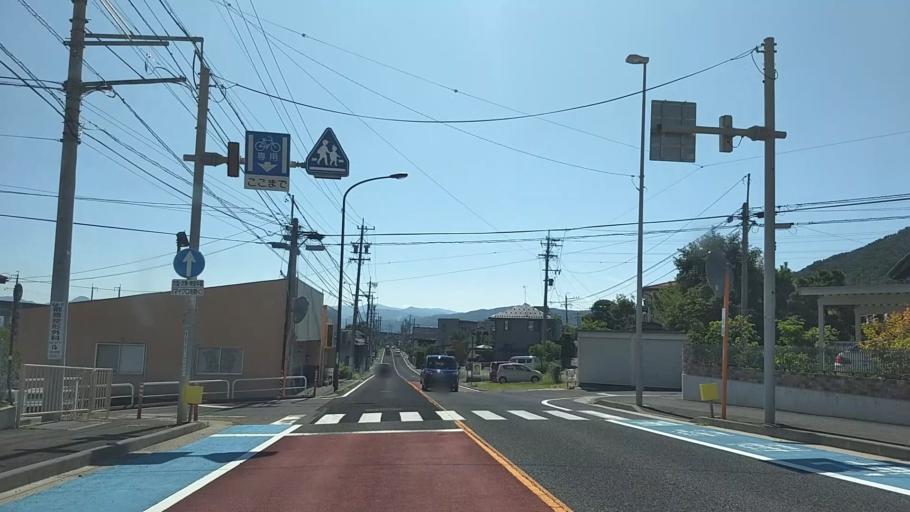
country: JP
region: Nagano
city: Nagano-shi
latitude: 36.6377
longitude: 138.1719
